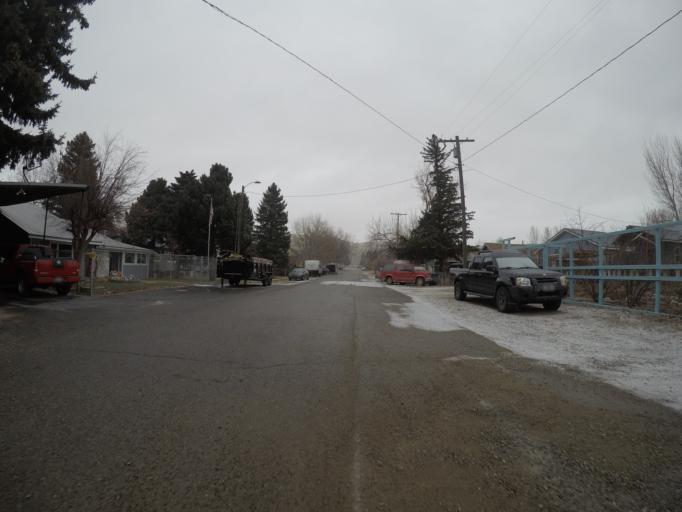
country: US
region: Montana
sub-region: Stillwater County
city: Absarokee
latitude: 45.5178
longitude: -109.4489
